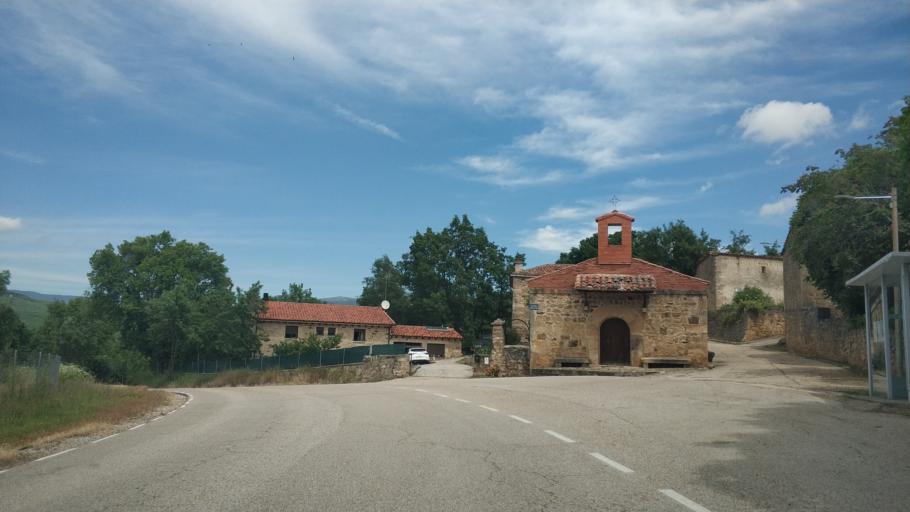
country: ES
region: Castille and Leon
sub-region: Provincia de Soria
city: Sotillo del Rincon
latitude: 41.8964
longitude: -2.6378
